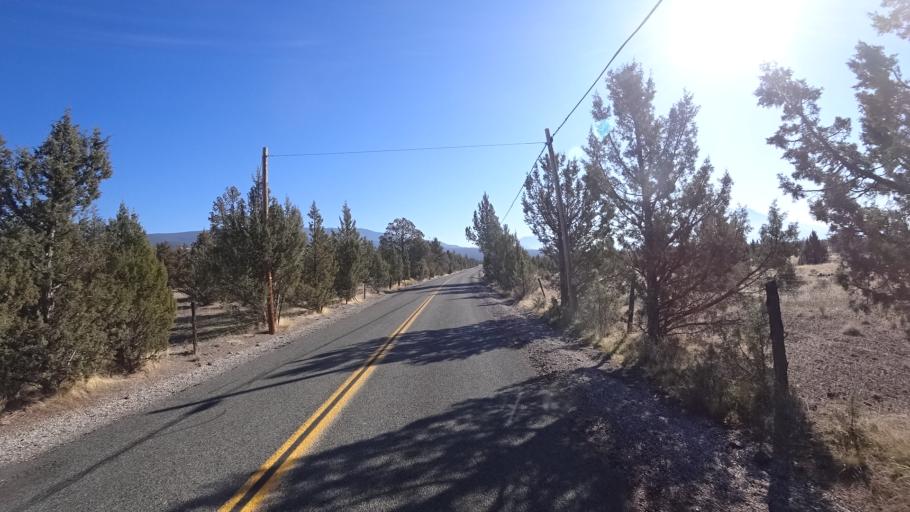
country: US
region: California
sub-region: Siskiyou County
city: Montague
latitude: 41.6458
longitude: -122.3566
